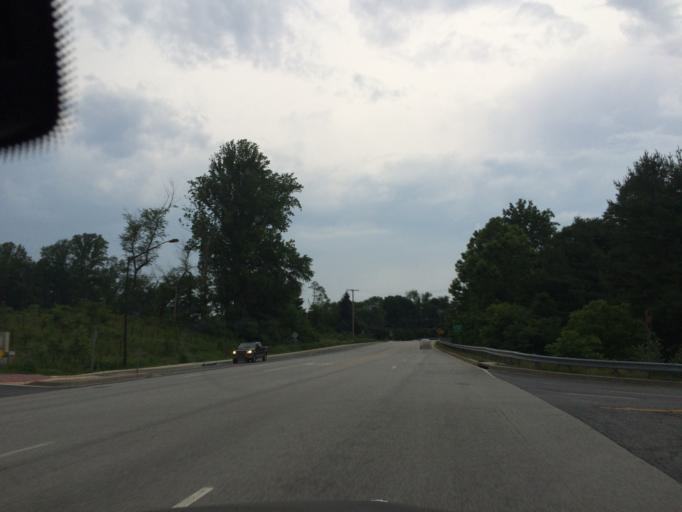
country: US
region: Maryland
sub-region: Howard County
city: Riverside
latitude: 39.1889
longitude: -76.8935
